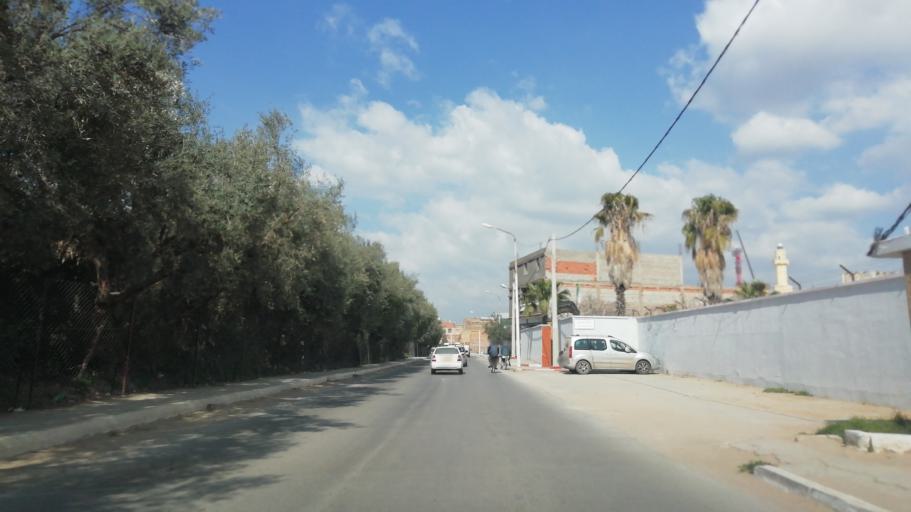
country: DZ
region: Mascara
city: Mascara
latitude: 35.5761
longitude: 0.0703
